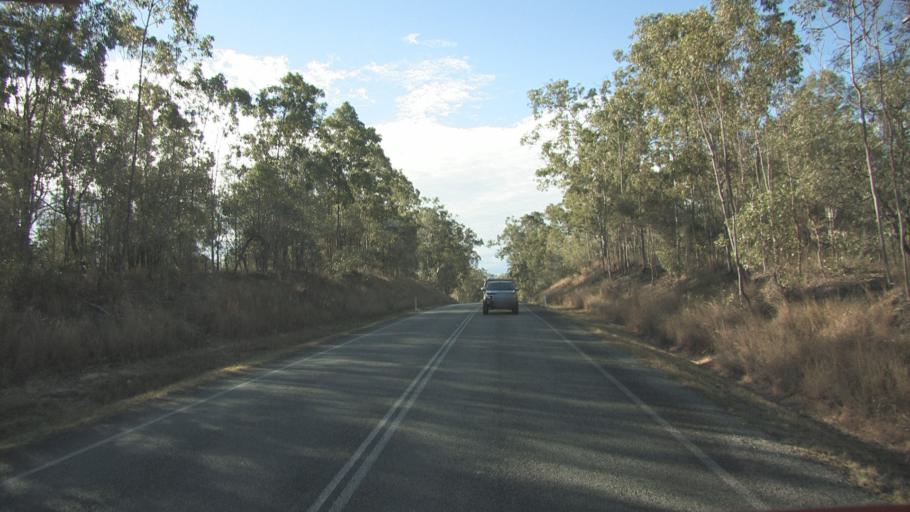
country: AU
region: Queensland
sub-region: Logan
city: Cedar Vale
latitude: -27.9080
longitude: 153.0899
